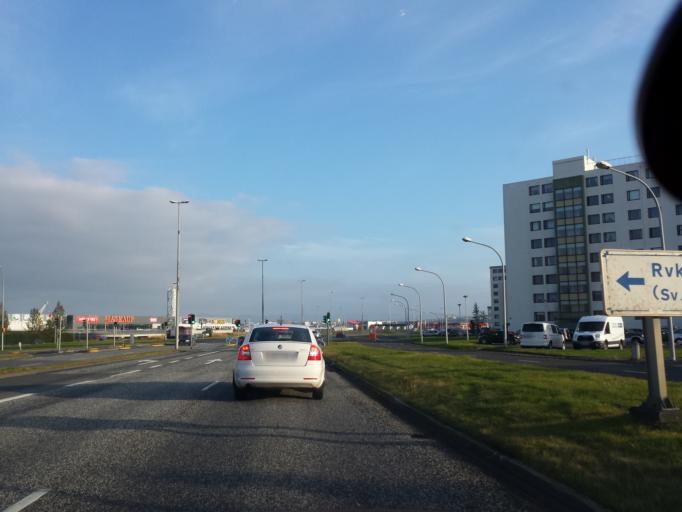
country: IS
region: Capital Region
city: Reykjavik
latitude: 64.1439
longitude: -21.8539
